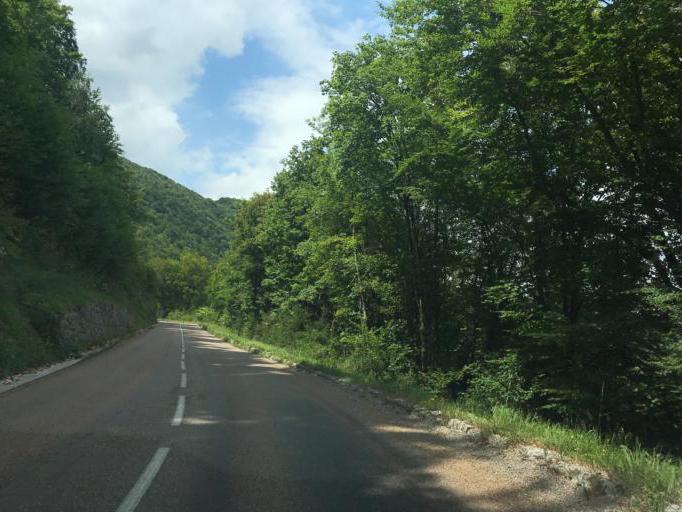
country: FR
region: Franche-Comte
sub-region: Departement du Jura
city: Valfin-les-Saint-Claude
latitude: 46.4189
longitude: 5.8622
